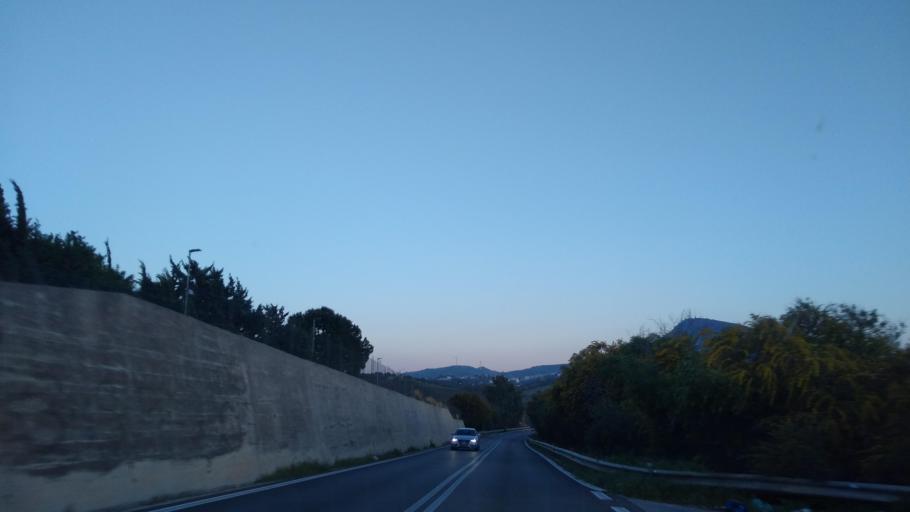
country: IT
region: Sicily
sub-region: Trapani
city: Alcamo
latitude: 38.0114
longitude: 12.9611
